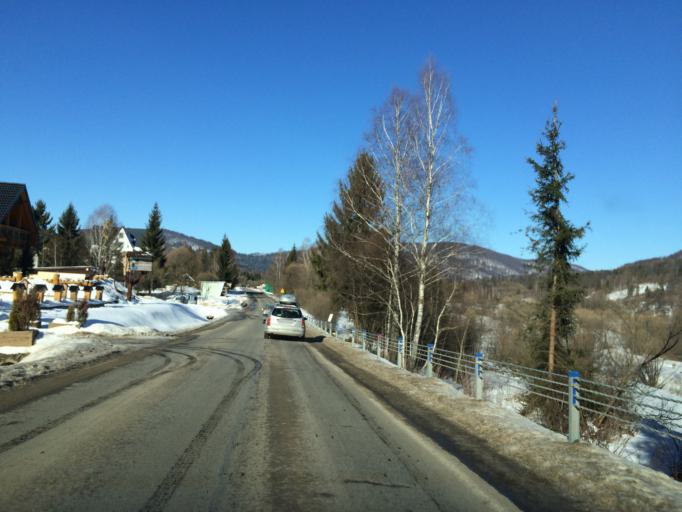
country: PL
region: Subcarpathian Voivodeship
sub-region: Powiat leski
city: Cisna
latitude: 49.1751
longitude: 22.4402
